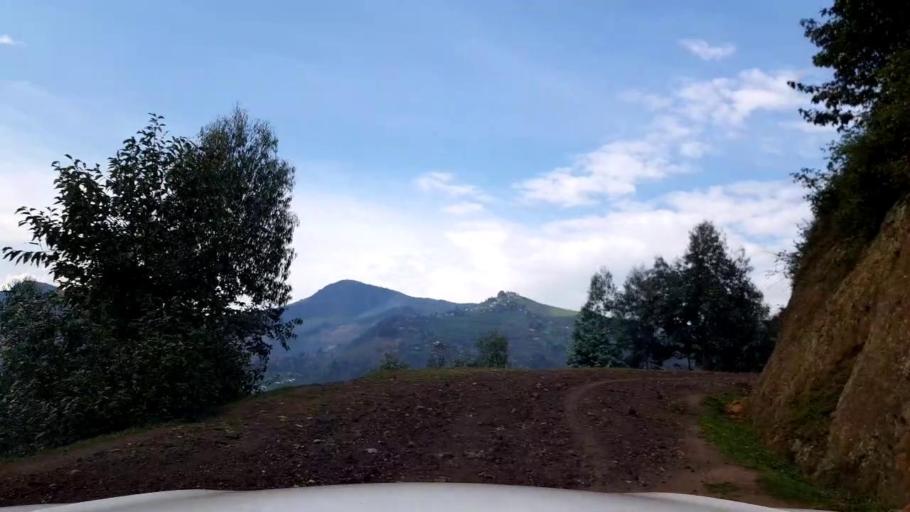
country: RW
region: Western Province
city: Gisenyi
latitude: -1.7176
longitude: 29.3882
